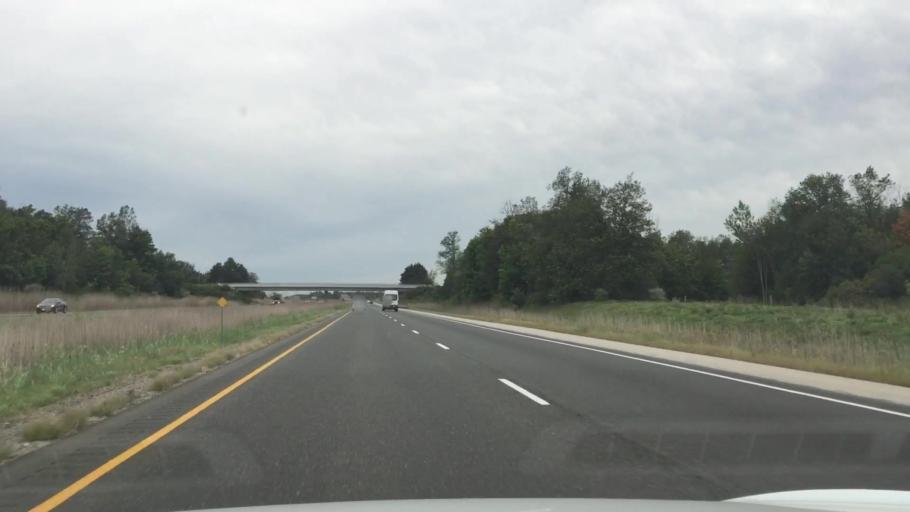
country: CA
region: Ontario
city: Delaware
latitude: 42.8860
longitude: -81.3251
